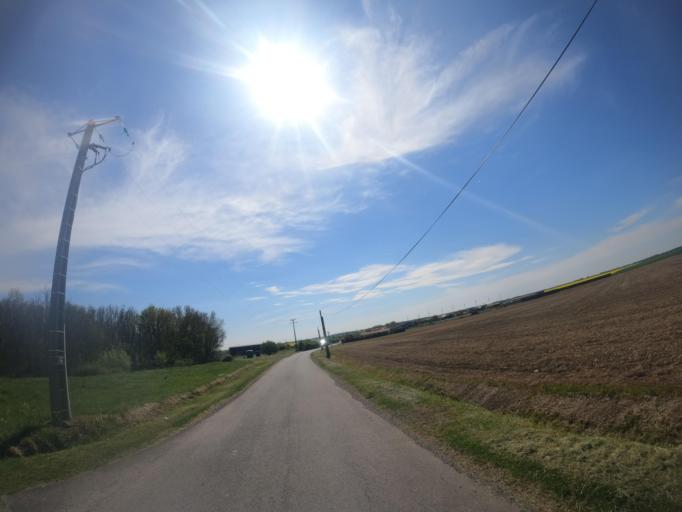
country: FR
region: Poitou-Charentes
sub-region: Departement des Deux-Sevres
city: Airvault
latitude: 46.8812
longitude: -0.1610
